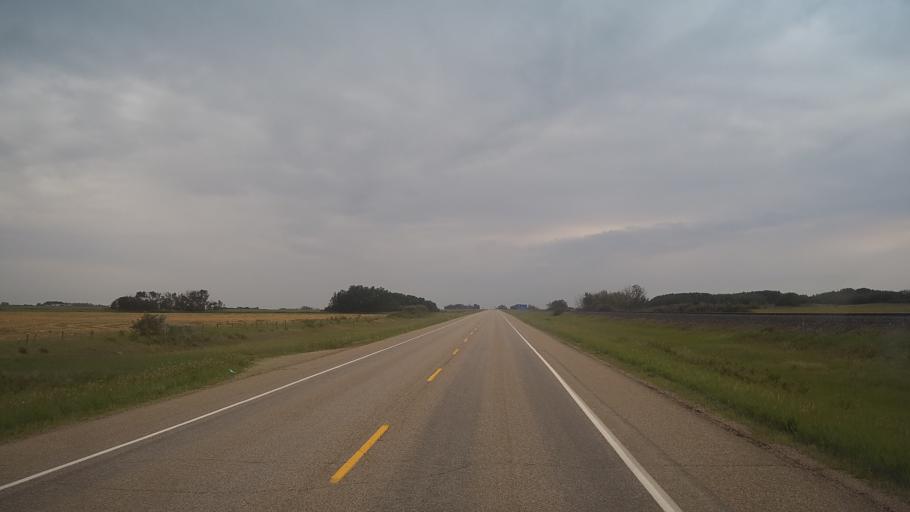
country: CA
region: Saskatchewan
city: Langham
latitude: 52.1268
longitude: -107.2719
